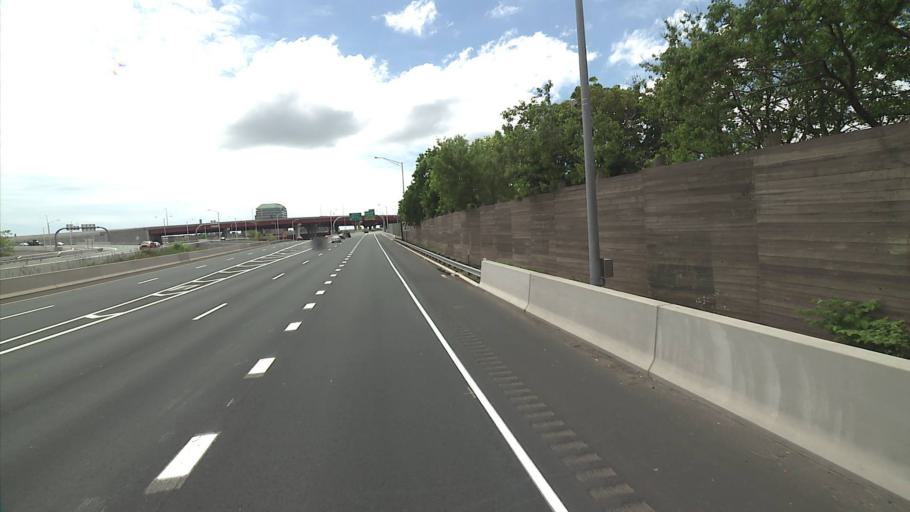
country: US
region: Connecticut
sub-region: New Haven County
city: New Haven
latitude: 41.3047
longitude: -72.9144
